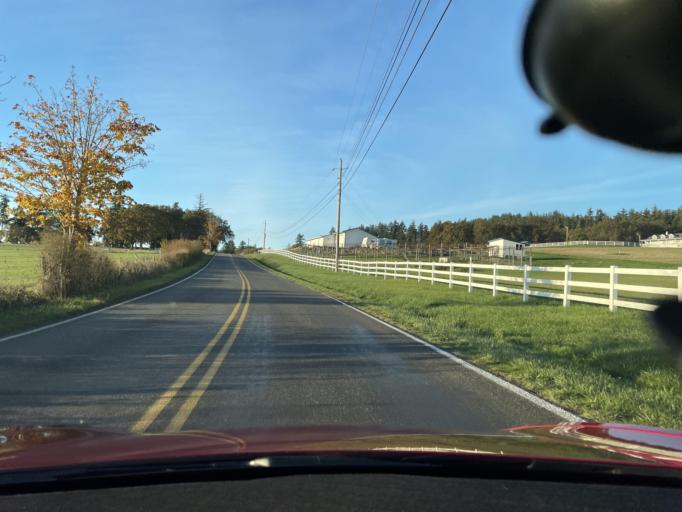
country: US
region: Washington
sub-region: San Juan County
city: Friday Harbor
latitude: 48.5737
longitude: -123.1391
